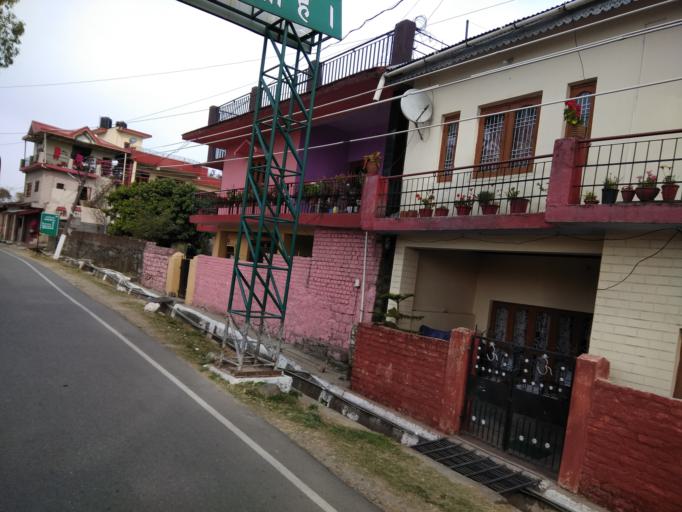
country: IN
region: Himachal Pradesh
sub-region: Kangra
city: Dharmsala
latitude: 32.1863
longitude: 76.3645
